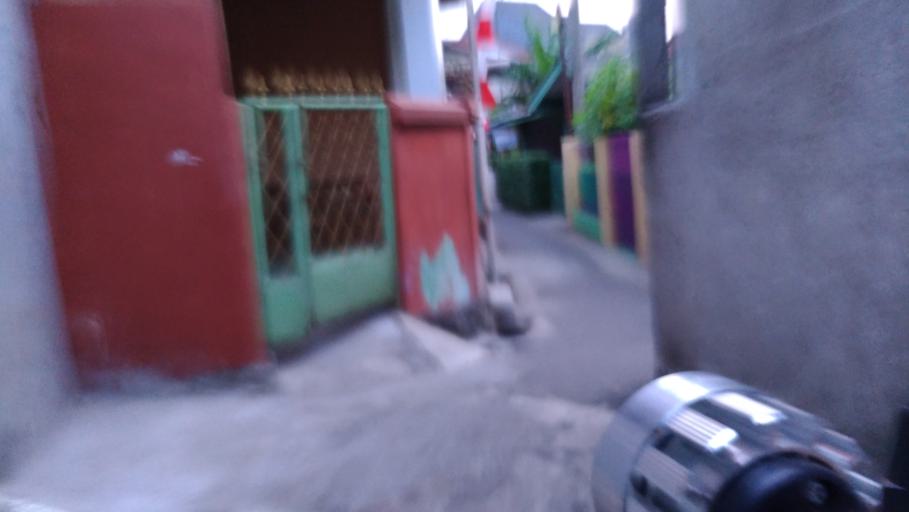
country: ID
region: West Java
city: Depok
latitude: -6.3497
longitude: 106.8706
